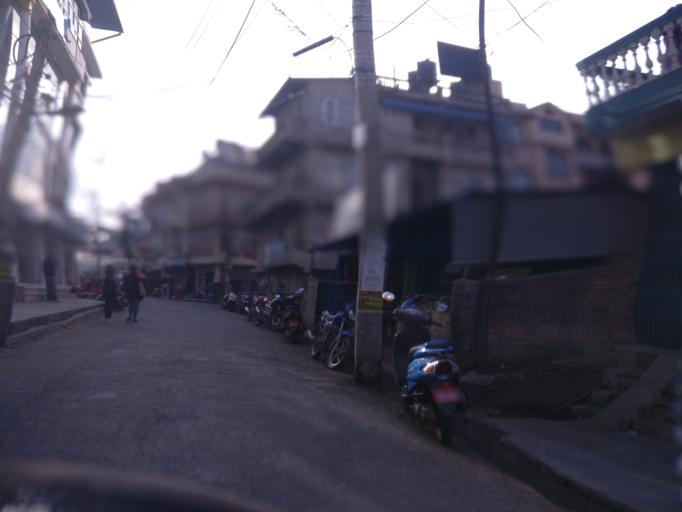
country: NP
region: Central Region
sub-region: Bagmati Zone
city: Patan
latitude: 27.6547
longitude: 85.3197
